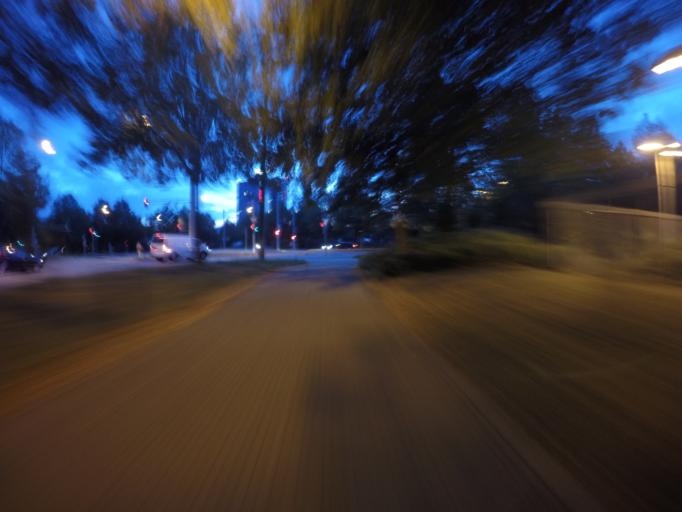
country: DE
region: Baden-Wuerttemberg
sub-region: Regierungsbezirk Stuttgart
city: Leinfelden-Echterdingen
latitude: 48.7225
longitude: 9.1672
